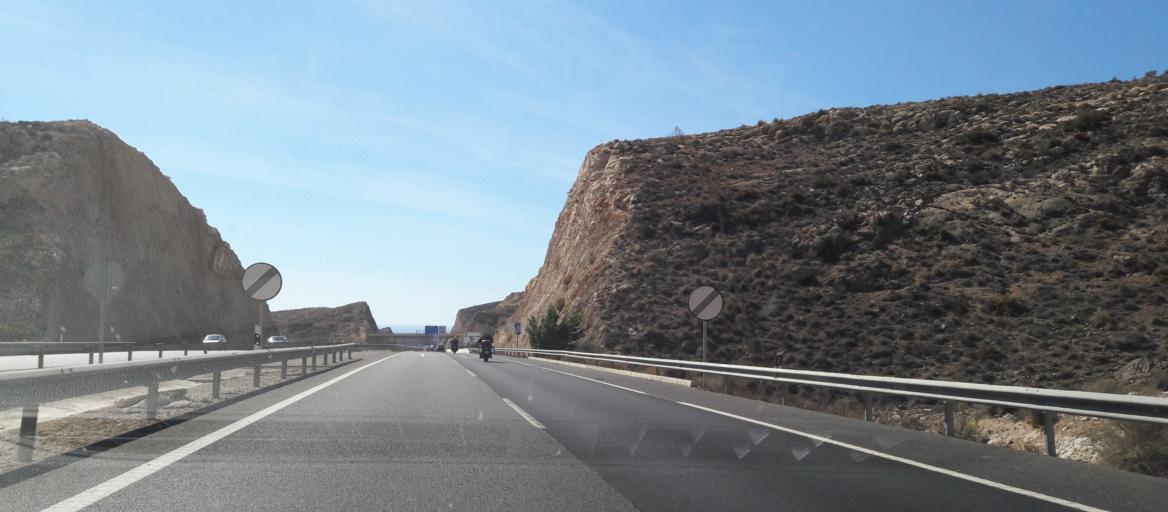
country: ES
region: Andalusia
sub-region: Provincia de Almeria
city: Huercal de Almeria
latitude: 36.8783
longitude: -2.4590
